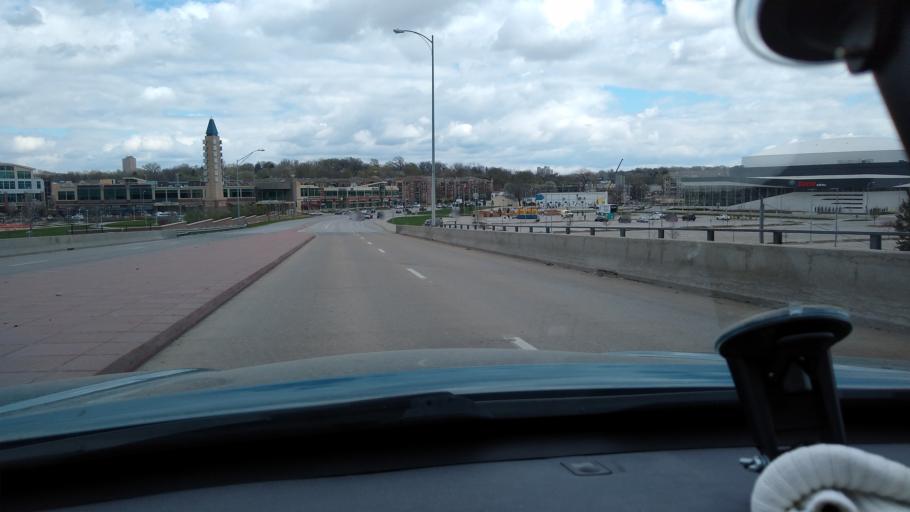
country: US
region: Nebraska
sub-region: Douglas County
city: Ralston
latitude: 41.2368
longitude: -96.0169
